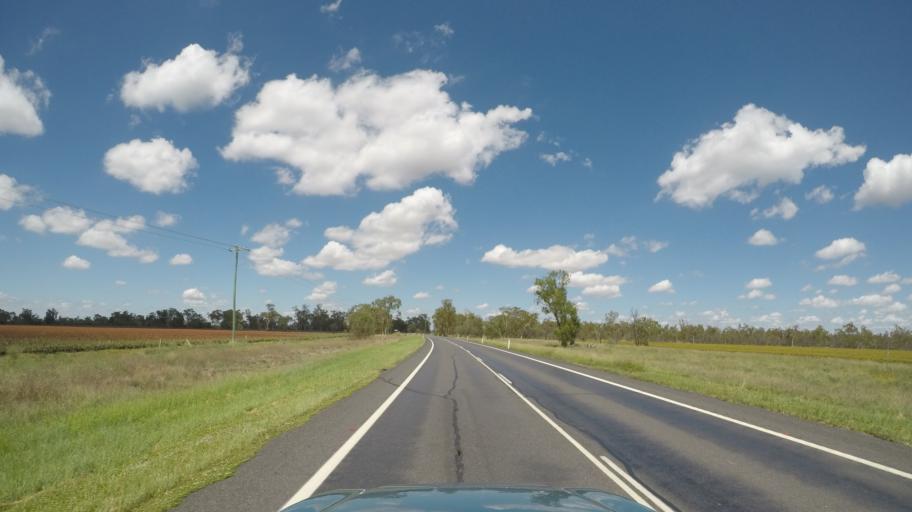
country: AU
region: Queensland
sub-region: Toowoomba
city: Oakey
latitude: -27.8071
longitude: 151.3654
